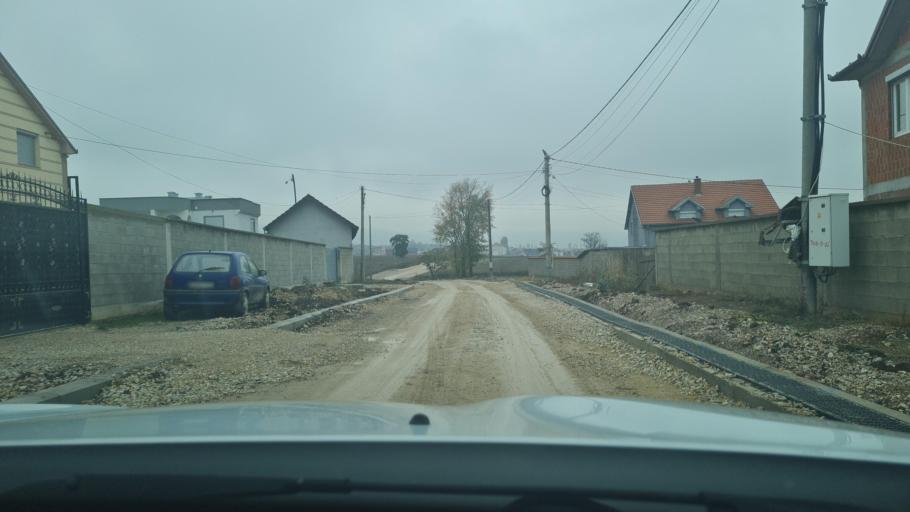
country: MK
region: Opstina Lipkovo
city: Matejche
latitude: 42.1129
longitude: 21.6120
